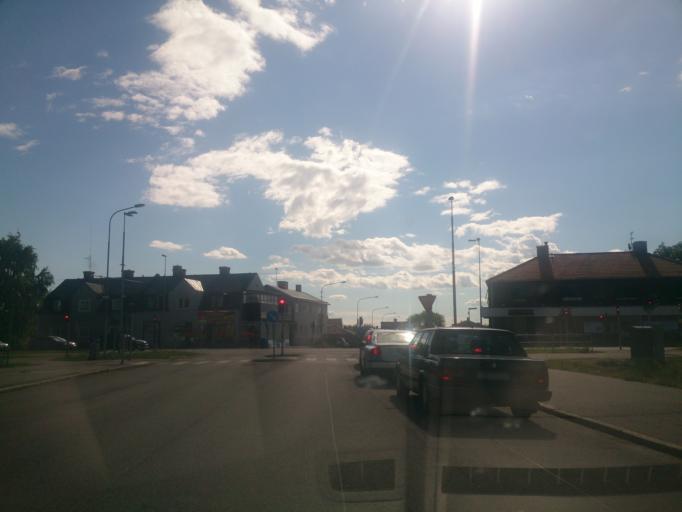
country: SE
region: OEstergoetland
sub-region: Norrkopings Kommun
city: Norrkoping
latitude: 58.6064
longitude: 16.1395
